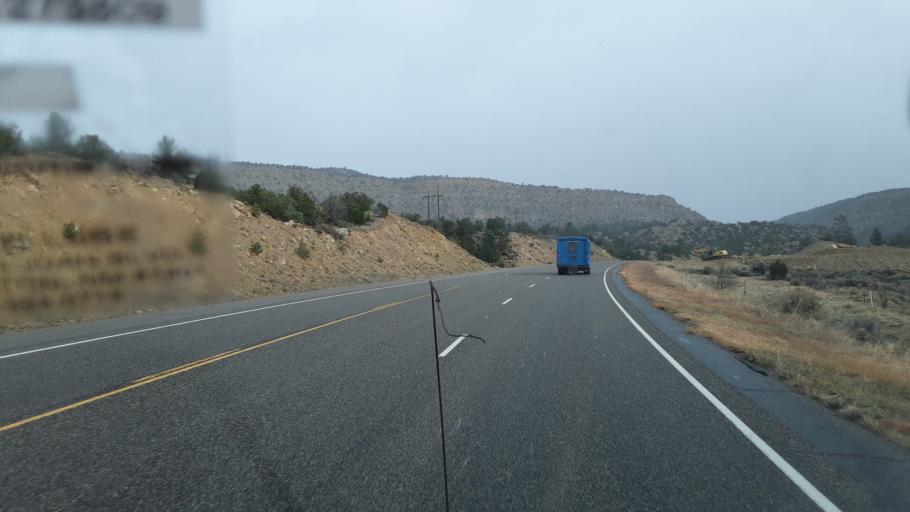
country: US
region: New Mexico
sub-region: Rio Arriba County
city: Tierra Amarilla
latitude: 36.4019
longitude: -106.4945
